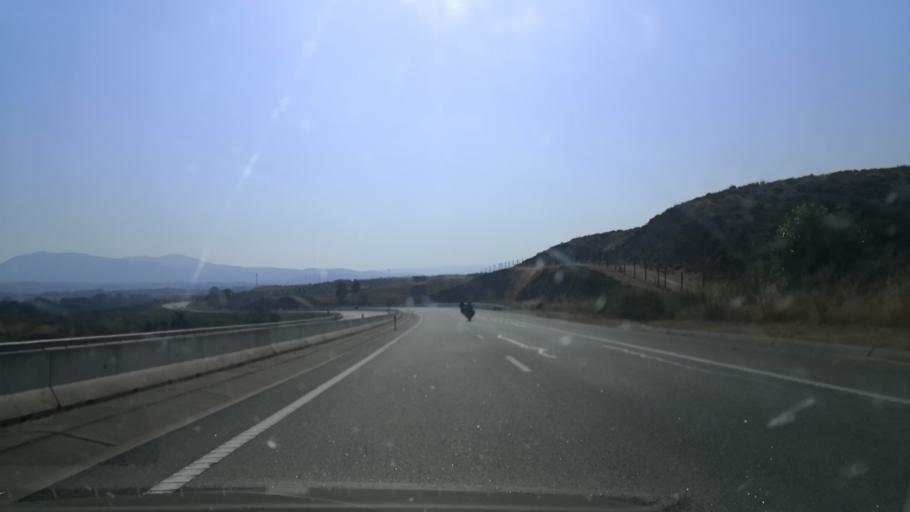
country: PT
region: Braganca
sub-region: Mirandela
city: Mirandela
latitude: 41.5187
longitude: -7.1434
